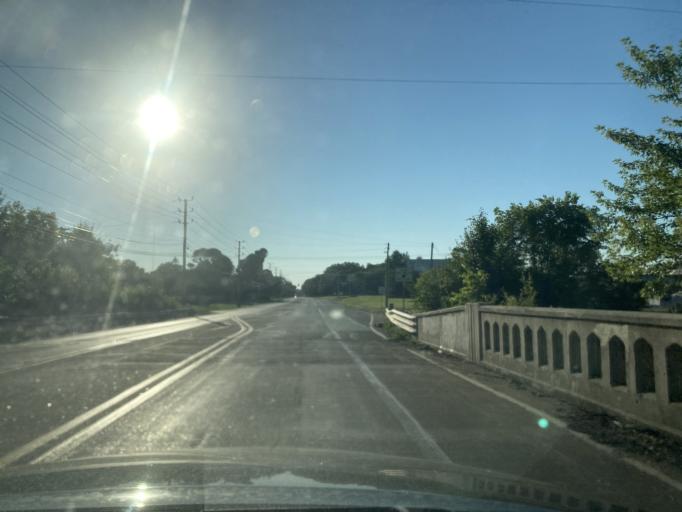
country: US
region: Indiana
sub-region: Boone County
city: Zionsville
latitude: 39.8823
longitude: -86.2344
